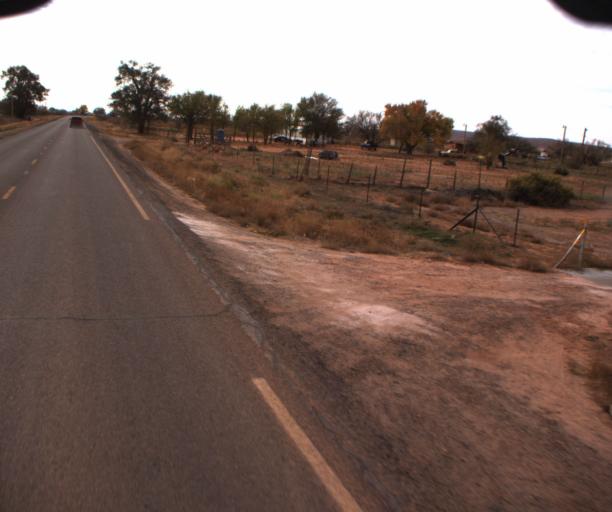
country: US
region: Arizona
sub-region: Apache County
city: Chinle
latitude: 36.2387
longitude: -109.6011
